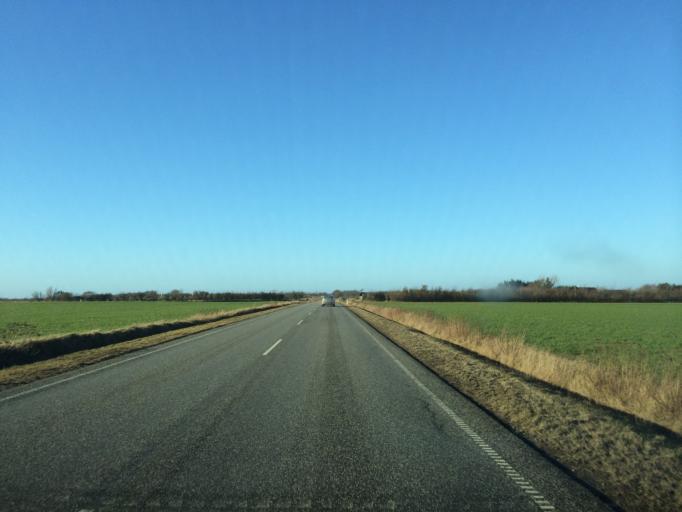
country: DK
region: Central Jutland
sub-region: Ringkobing-Skjern Kommune
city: Ringkobing
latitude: 56.0969
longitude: 8.3346
